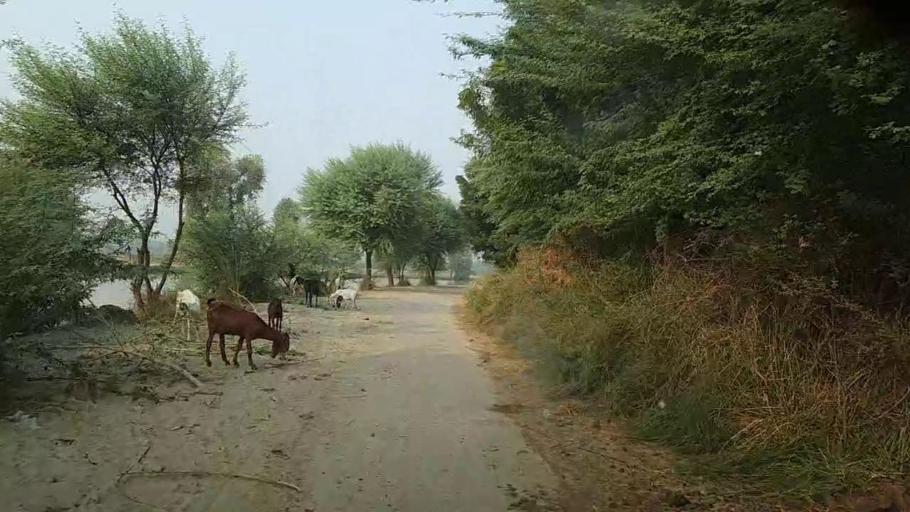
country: PK
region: Sindh
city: Bozdar
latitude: 27.1620
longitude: 68.6608
